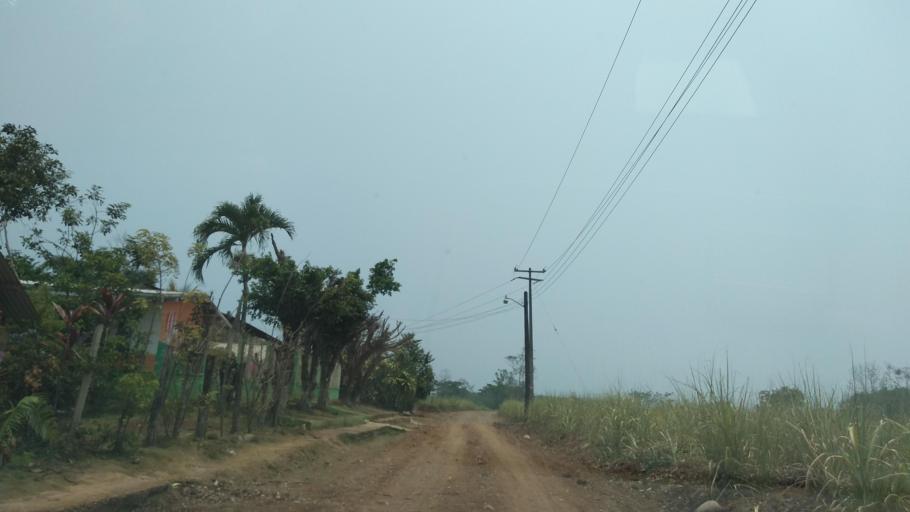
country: MX
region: Puebla
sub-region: San Sebastian Tlacotepec
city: San Martin Mazateopan
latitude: 18.4964
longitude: -96.7799
